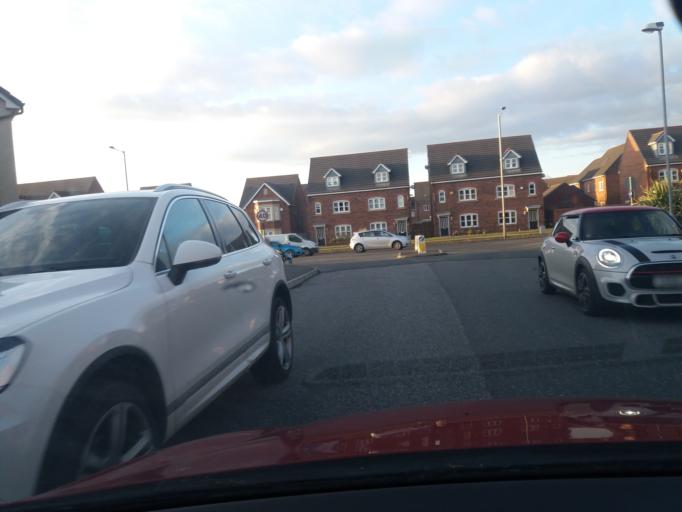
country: GB
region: England
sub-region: Lancashire
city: Euxton
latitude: 53.6765
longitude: -2.6606
